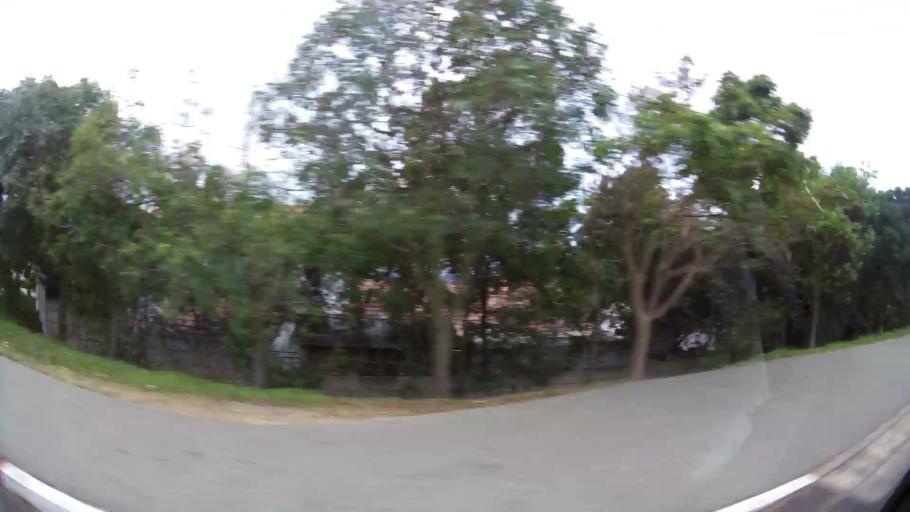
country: ZA
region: Western Cape
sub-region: Eden District Municipality
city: Plettenberg Bay
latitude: -34.0515
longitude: 23.3616
